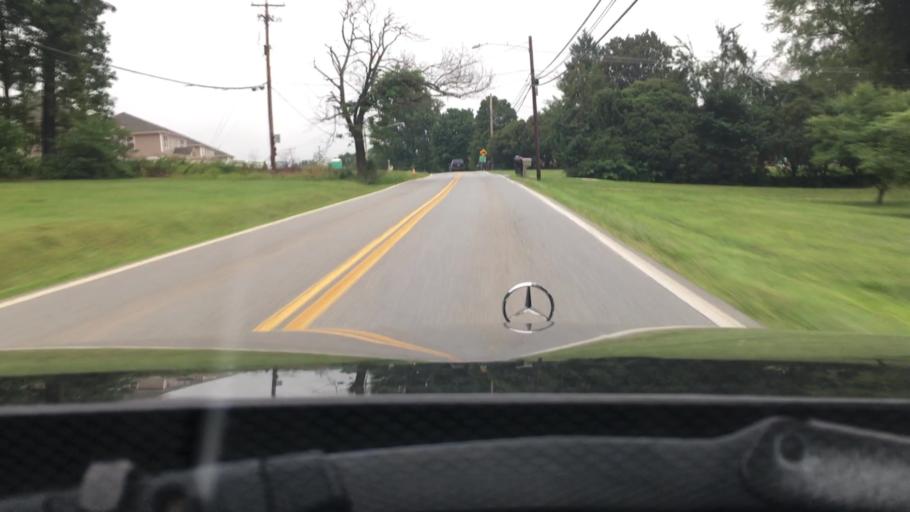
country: US
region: Virginia
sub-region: Campbell County
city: Timberlake
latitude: 37.3645
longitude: -79.2277
